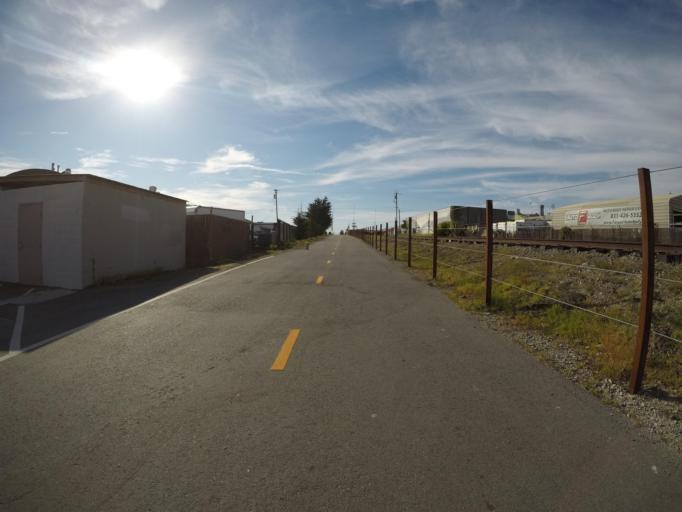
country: US
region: California
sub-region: Santa Cruz County
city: Santa Cruz
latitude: 36.9594
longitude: -122.0480
